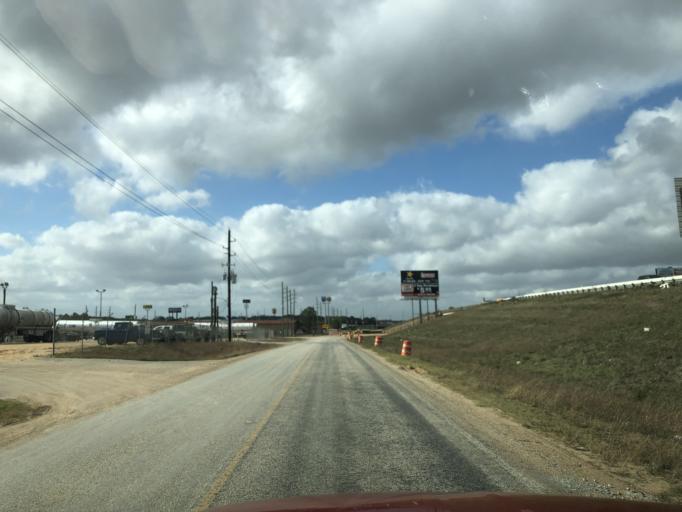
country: US
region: Texas
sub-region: Austin County
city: Sealy
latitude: 29.7654
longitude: -96.1485
